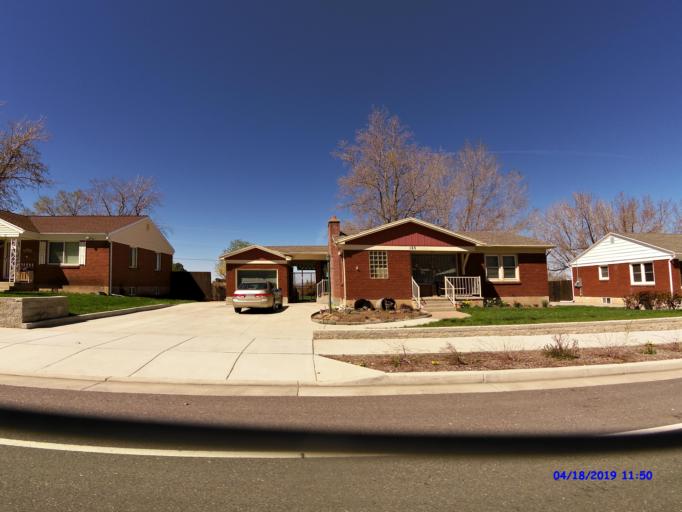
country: US
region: Utah
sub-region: Weber County
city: Ogden
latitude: 41.2601
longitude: -111.9479
